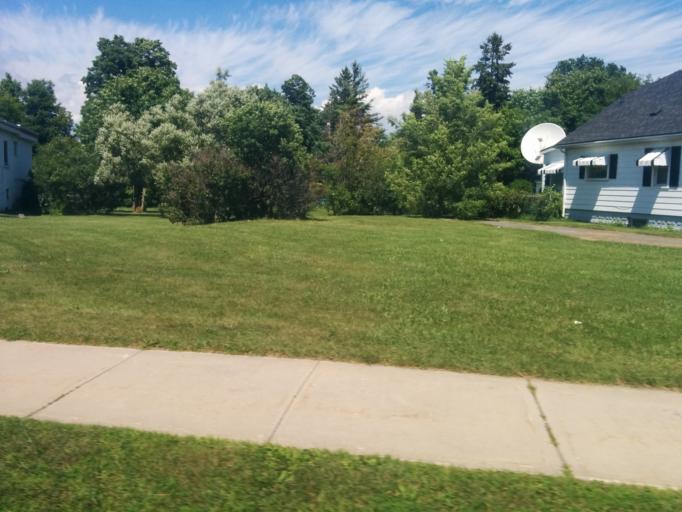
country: CA
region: Ontario
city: Kingston
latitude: 44.2486
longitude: -76.5274
